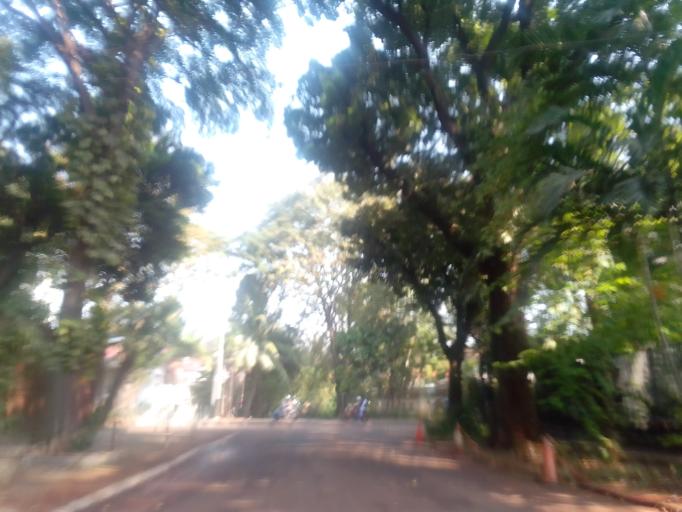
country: ID
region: Jakarta Raya
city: Jakarta
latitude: -6.2538
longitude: 106.8037
